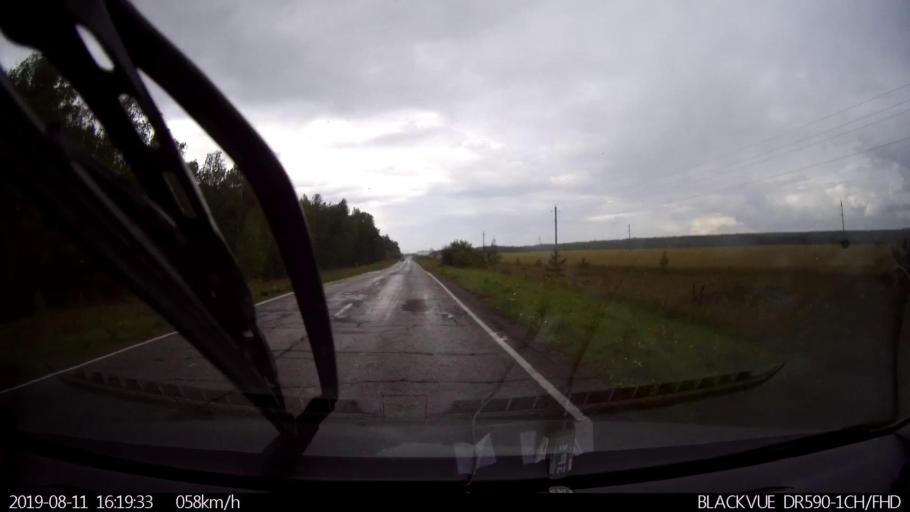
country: RU
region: Ulyanovsk
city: Mayna
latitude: 54.0647
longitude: 47.6068
